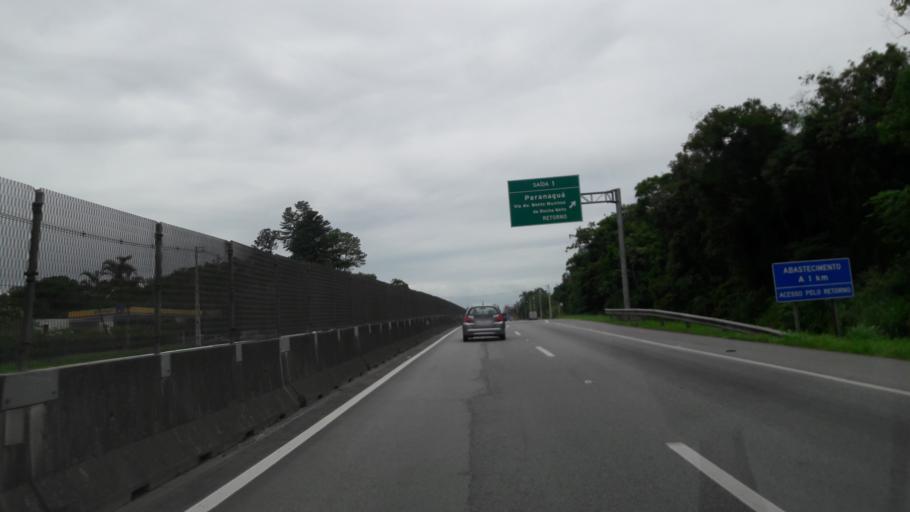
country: BR
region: Parana
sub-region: Paranagua
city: Paranagua
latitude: -25.5664
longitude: -48.5781
